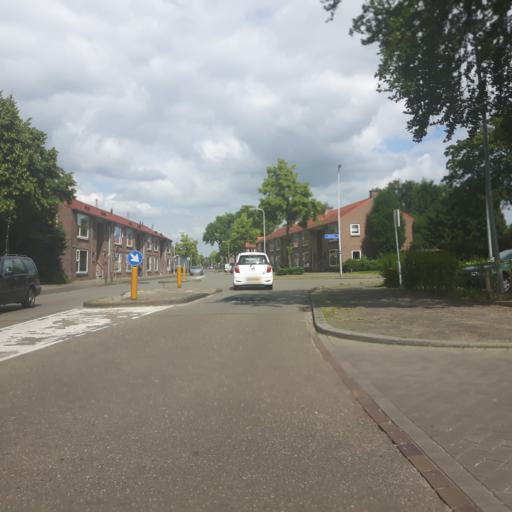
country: NL
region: Overijssel
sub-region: Gemeente Enschede
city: Enschede
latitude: 52.2134
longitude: 6.8616
